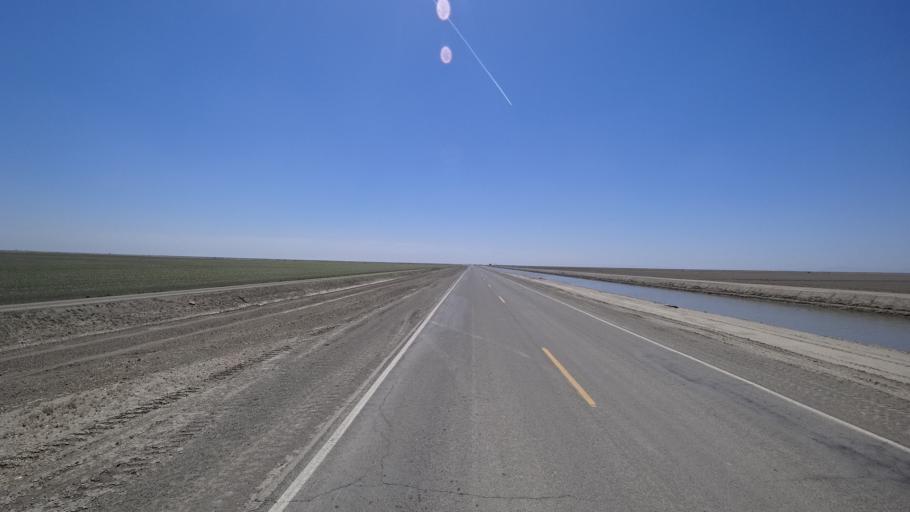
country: US
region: California
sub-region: Kings County
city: Corcoran
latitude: 36.0640
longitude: -119.6438
